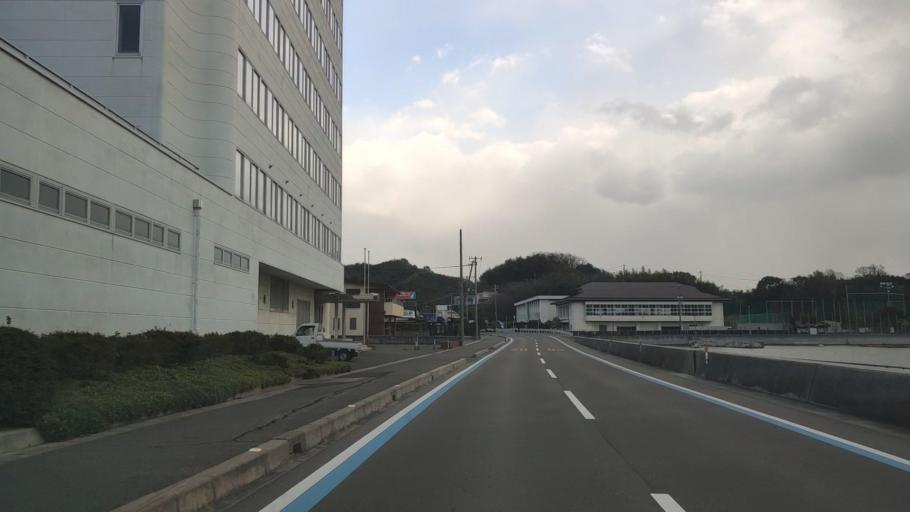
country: JP
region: Hiroshima
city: Innoshima
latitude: 34.2038
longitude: 133.0998
